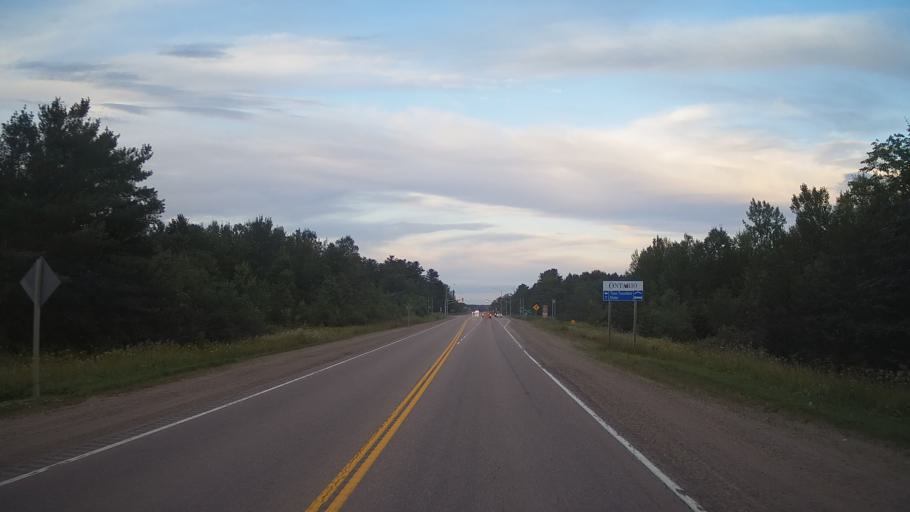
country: CA
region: Ontario
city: Pembroke
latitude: 45.7903
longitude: -77.1711
